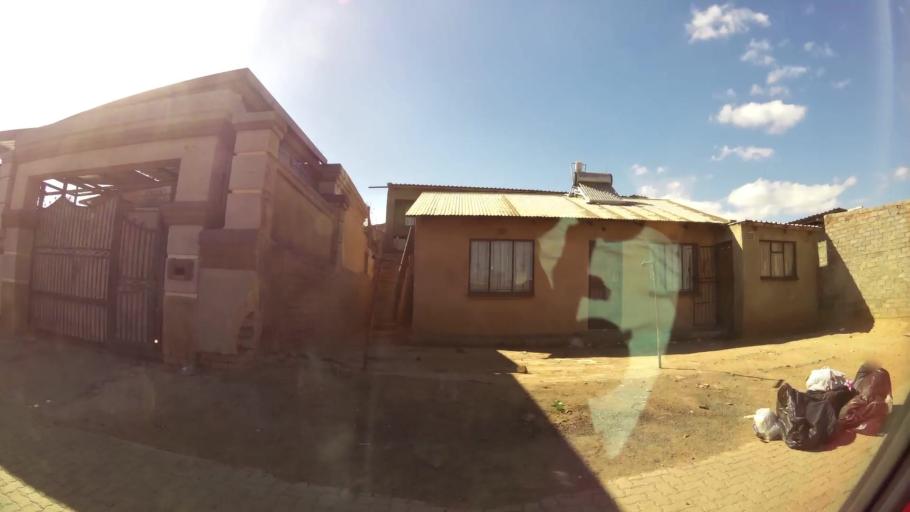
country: ZA
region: Gauteng
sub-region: City of Johannesburg Metropolitan Municipality
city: Midrand
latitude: -26.0295
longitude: 28.1707
